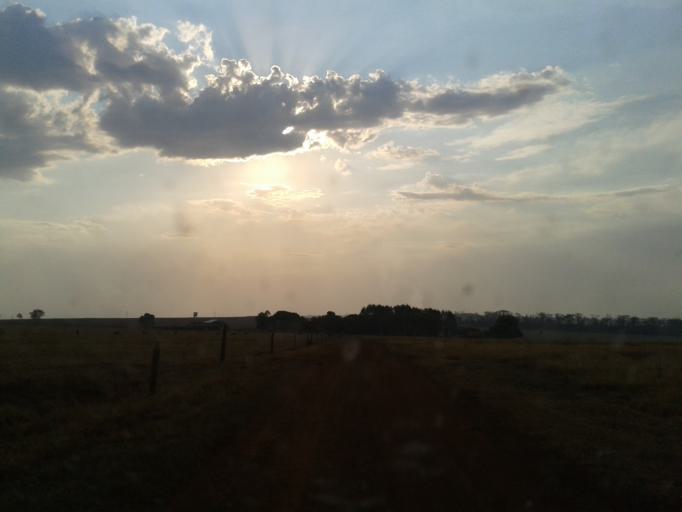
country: BR
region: Minas Gerais
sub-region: Capinopolis
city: Capinopolis
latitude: -18.7657
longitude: -49.7209
